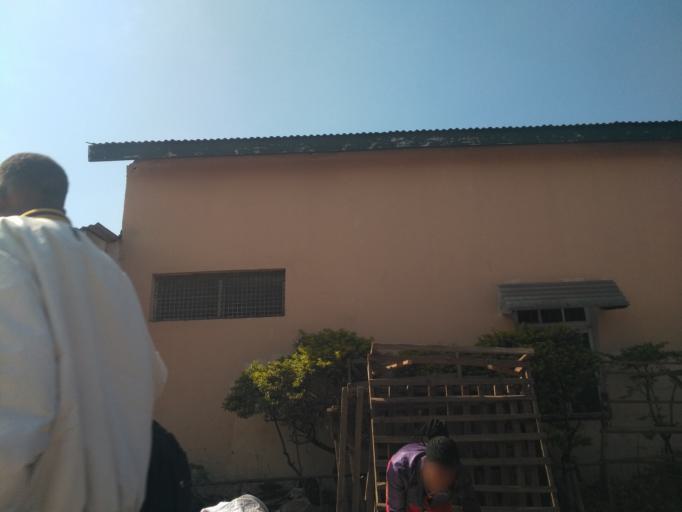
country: TZ
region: Arusha
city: Arusha
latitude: -3.3713
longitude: 36.6833
